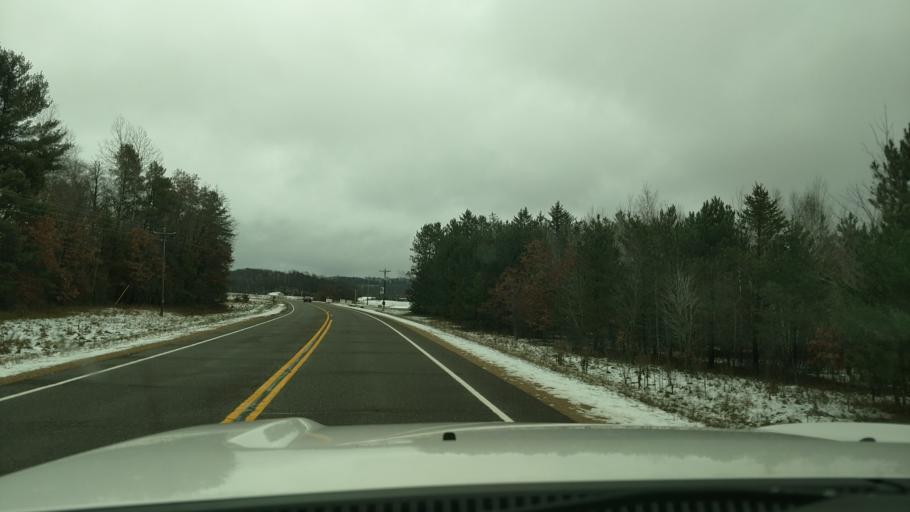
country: US
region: Wisconsin
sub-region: Dunn County
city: Tainter Lake
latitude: 45.1214
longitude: -91.8880
